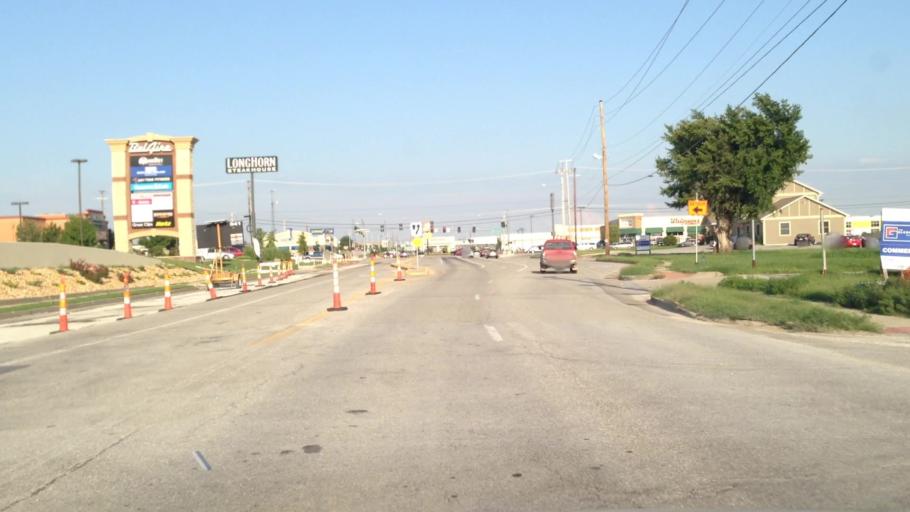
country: US
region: Missouri
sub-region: Jasper County
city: Duquesne
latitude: 37.0693
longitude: -94.4802
